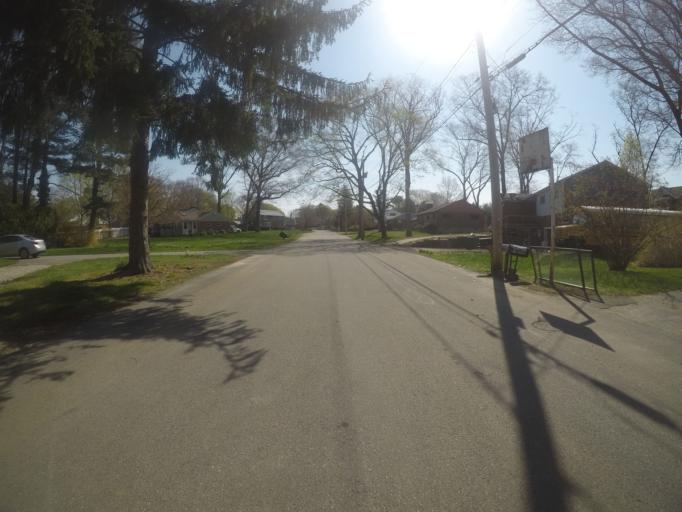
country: US
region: Massachusetts
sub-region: Bristol County
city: Easton
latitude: 42.0520
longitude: -71.0882
